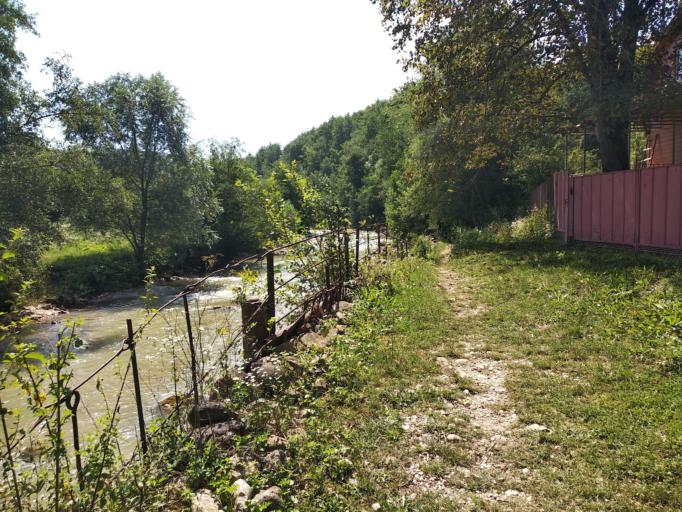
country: RU
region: Adygeya
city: Kamennomostskiy
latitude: 44.1988
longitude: 39.9566
